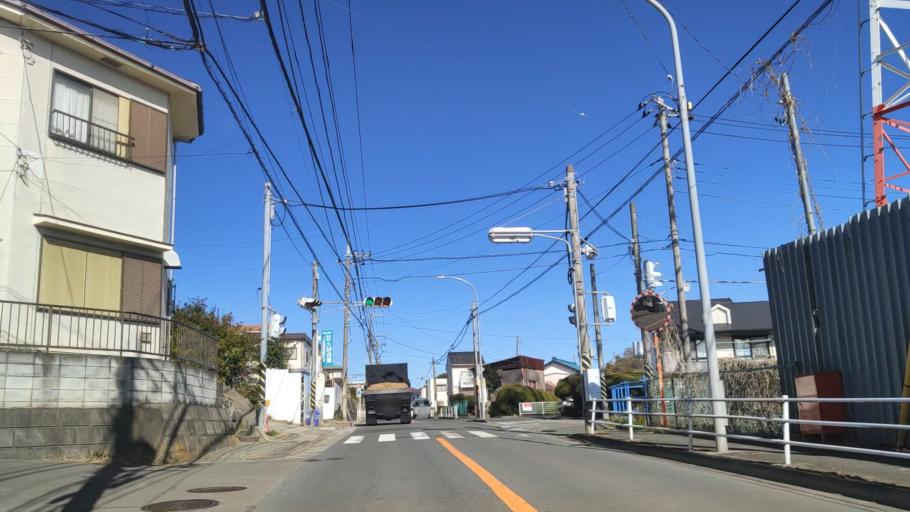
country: JP
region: Kanagawa
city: Minami-rinkan
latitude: 35.4925
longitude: 139.5166
